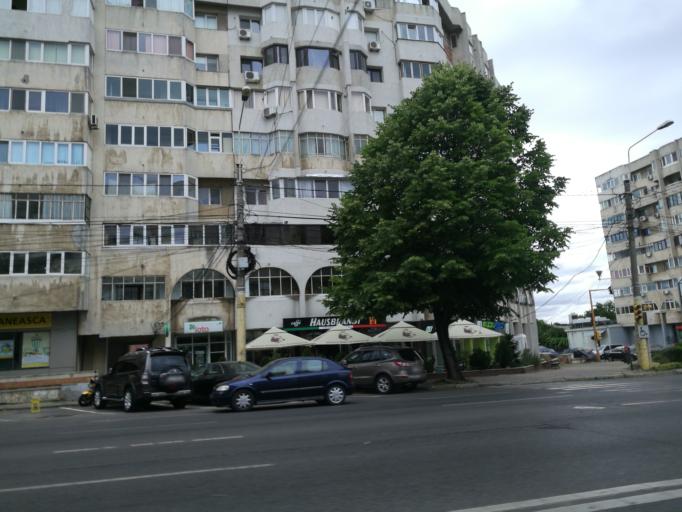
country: RO
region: Constanta
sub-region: Municipiul Constanta
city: Constanta
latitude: 44.1881
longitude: 28.6342
